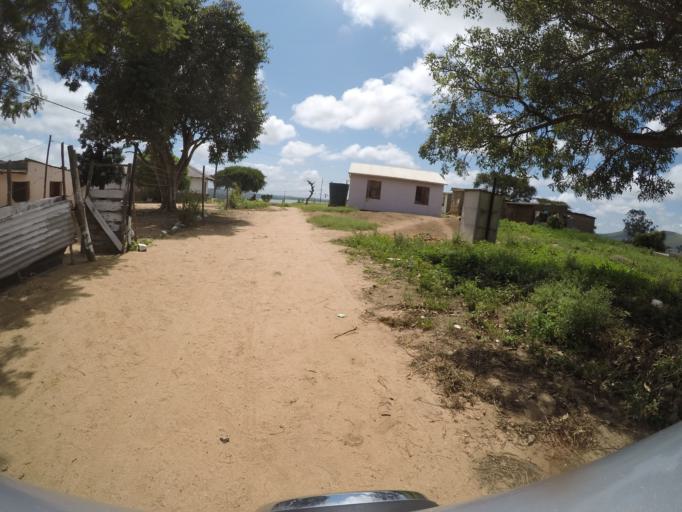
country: ZA
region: KwaZulu-Natal
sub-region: uThungulu District Municipality
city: Empangeni
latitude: -28.5780
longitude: 31.8424
